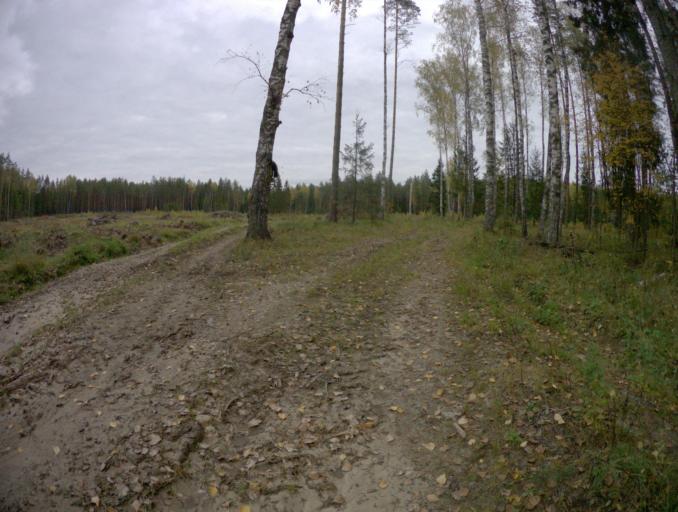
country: RU
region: Vladimir
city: Stepantsevo
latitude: 56.3111
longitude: 41.5677
